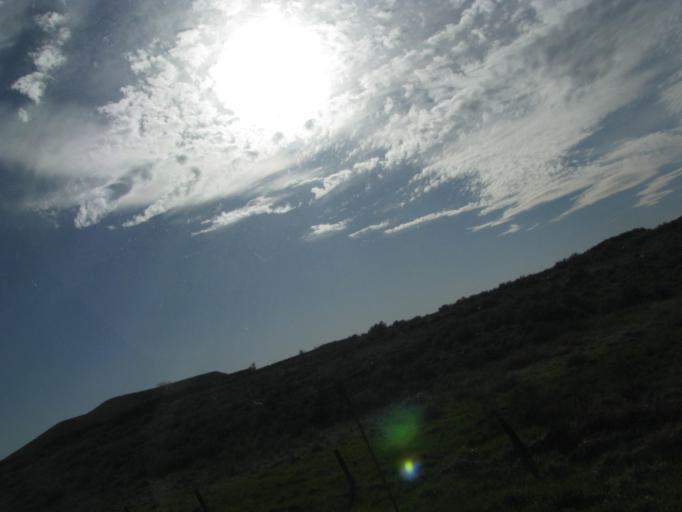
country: US
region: Washington
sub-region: Spokane County
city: Medical Lake
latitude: 47.3609
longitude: -117.8459
